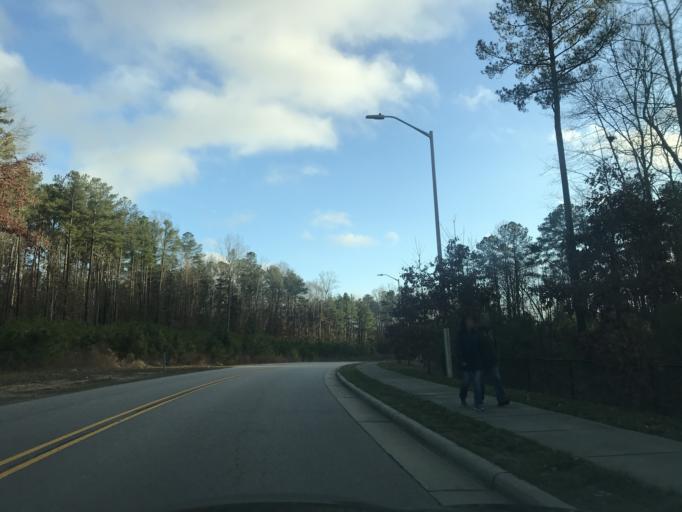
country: US
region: North Carolina
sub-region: Wake County
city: Wake Forest
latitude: 35.9557
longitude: -78.5337
